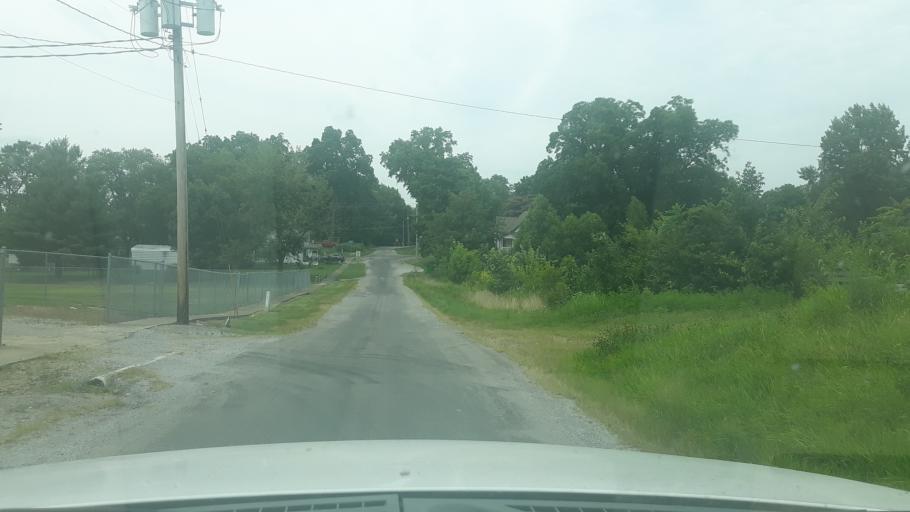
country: US
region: Illinois
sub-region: Saline County
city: Harrisburg
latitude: 37.8418
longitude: -88.6132
